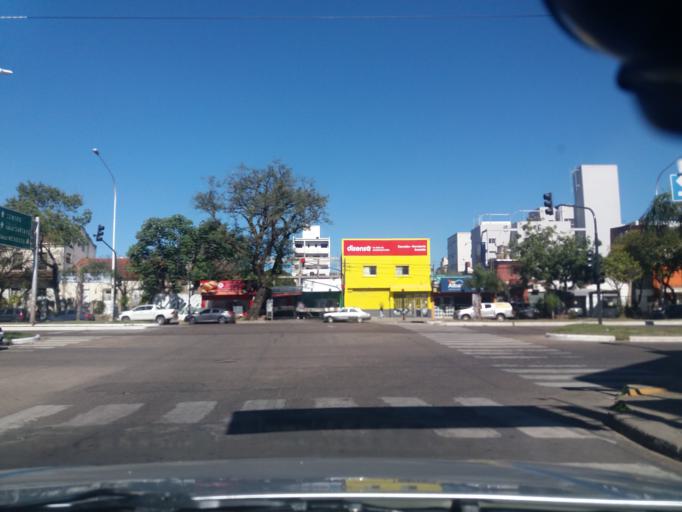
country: AR
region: Corrientes
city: Corrientes
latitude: -27.4751
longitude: -58.8397
